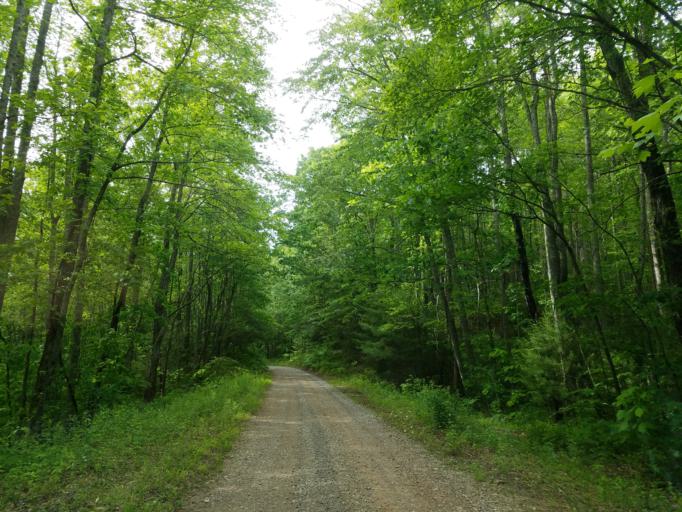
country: US
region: Georgia
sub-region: Union County
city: Blairsville
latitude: 34.7472
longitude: -83.9929
